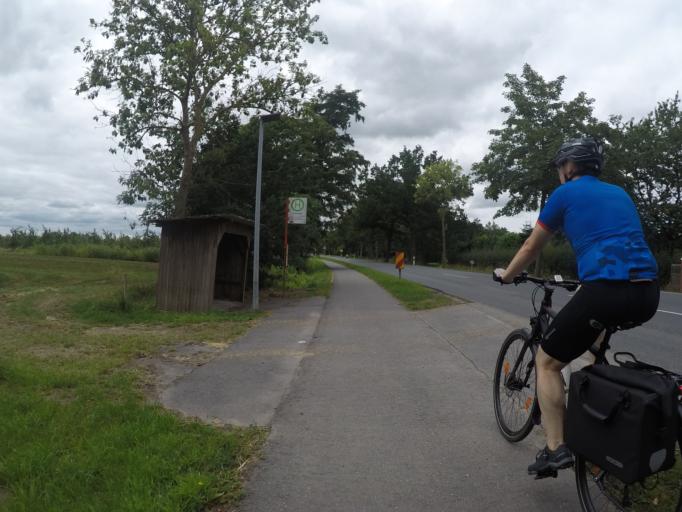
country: DE
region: Lower Saxony
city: Grossenworden
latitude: 53.6770
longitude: 9.2713
